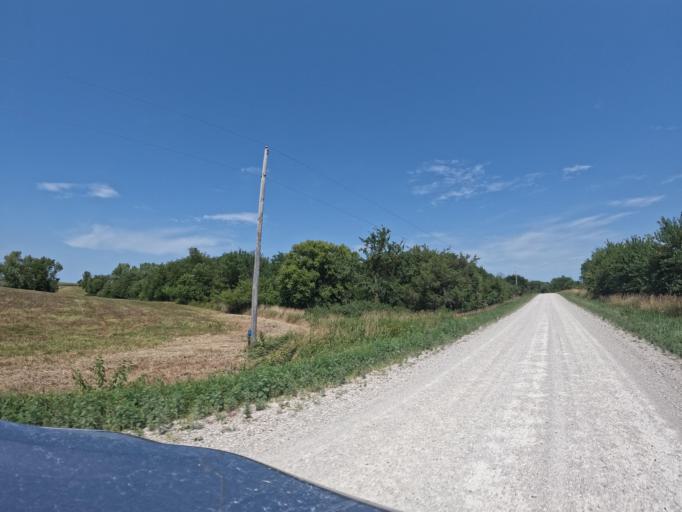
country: US
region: Iowa
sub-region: Henry County
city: Mount Pleasant
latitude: 40.8938
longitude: -91.6269
